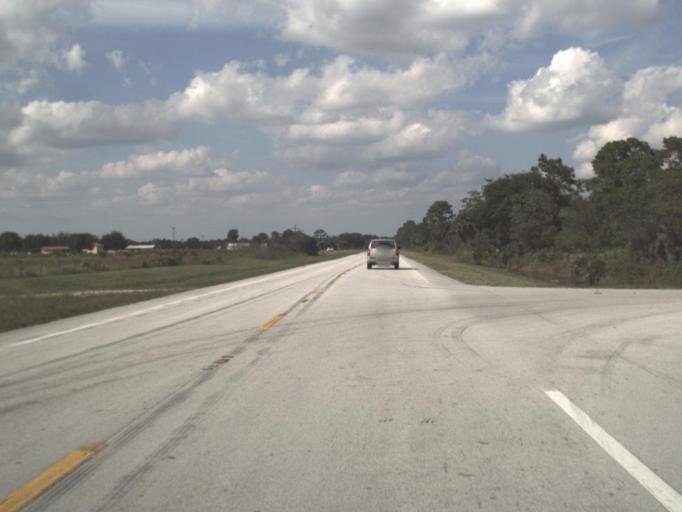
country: US
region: Florida
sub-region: Indian River County
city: Fellsmere
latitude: 27.5595
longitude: -80.8245
